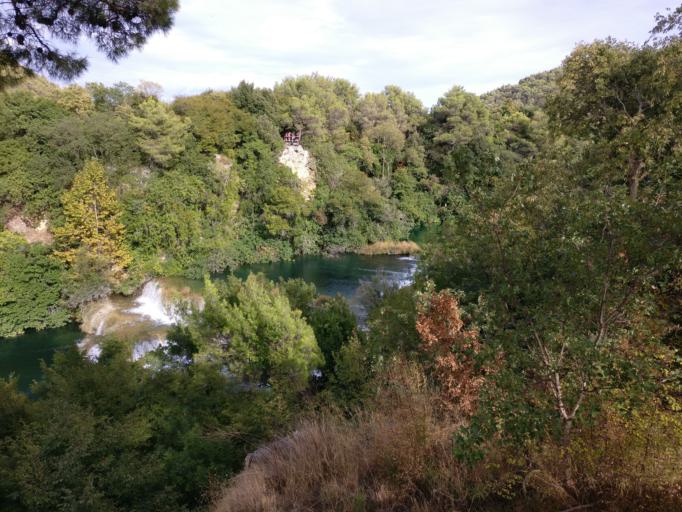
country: HR
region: Sibensko-Kniniska
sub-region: Grad Sibenik
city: Sibenik
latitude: 43.8043
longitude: 15.9638
